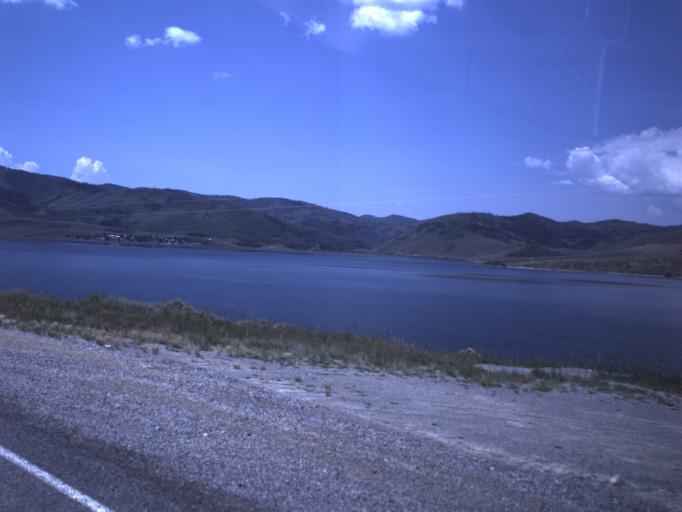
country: US
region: Utah
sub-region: Carbon County
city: Helper
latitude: 39.7866
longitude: -111.1332
